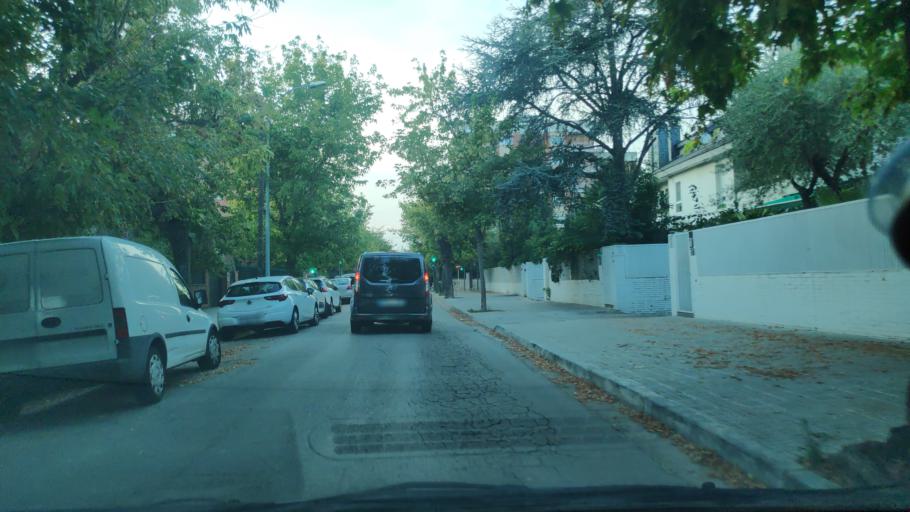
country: ES
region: Catalonia
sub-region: Provincia de Barcelona
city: Cerdanyola del Valles
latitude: 41.4877
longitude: 2.1348
